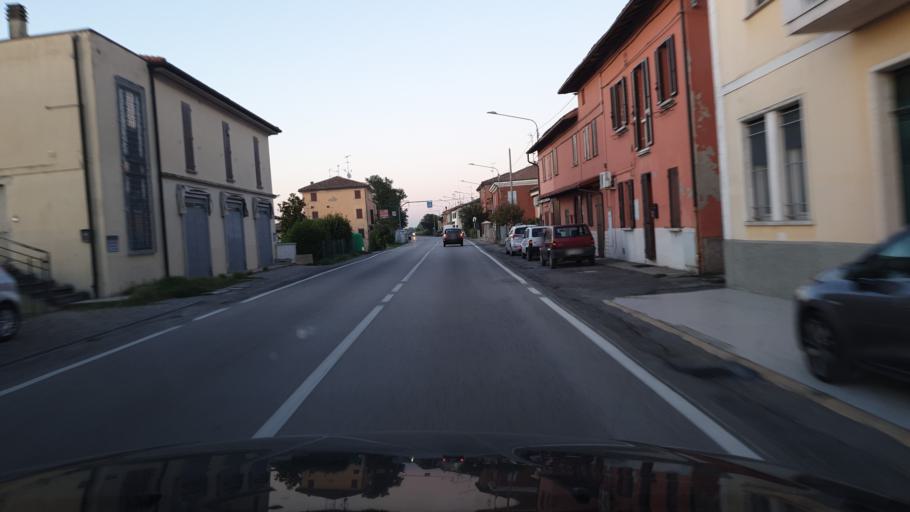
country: IT
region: Emilia-Romagna
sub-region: Provincia di Bologna
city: Ca De Fabbri
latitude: 44.6275
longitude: 11.4612
